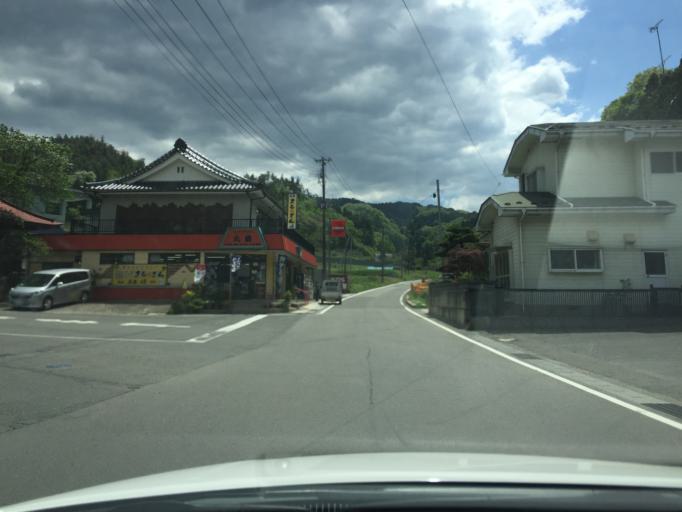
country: JP
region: Fukushima
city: Hobaramachi
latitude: 37.7341
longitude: 140.6323
